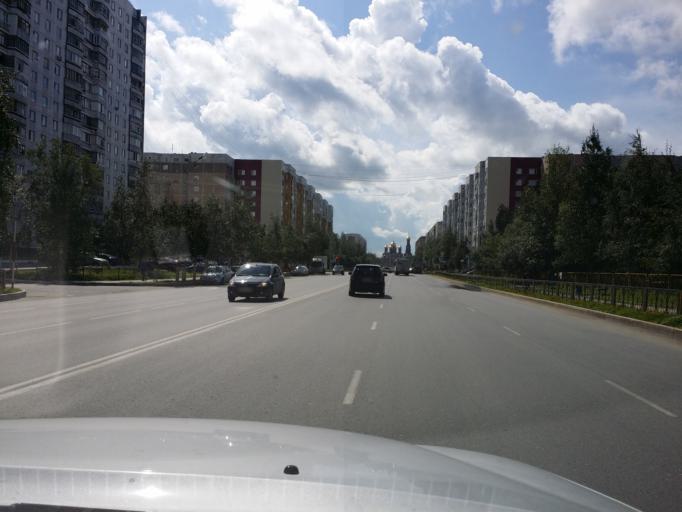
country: RU
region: Khanty-Mansiyskiy Avtonomnyy Okrug
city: Nizhnevartovsk
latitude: 60.9320
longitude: 76.5985
